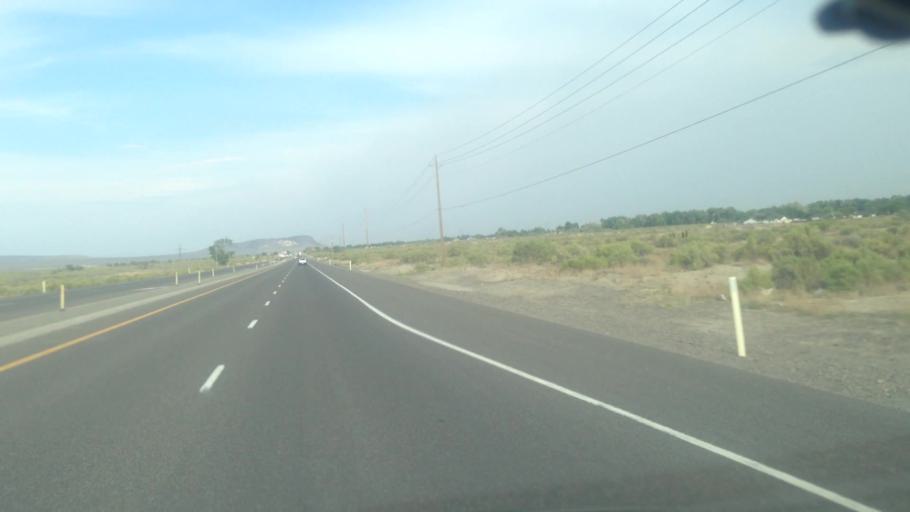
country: US
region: Nevada
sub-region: Lyon County
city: Fernley
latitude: 39.5966
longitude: -119.1853
